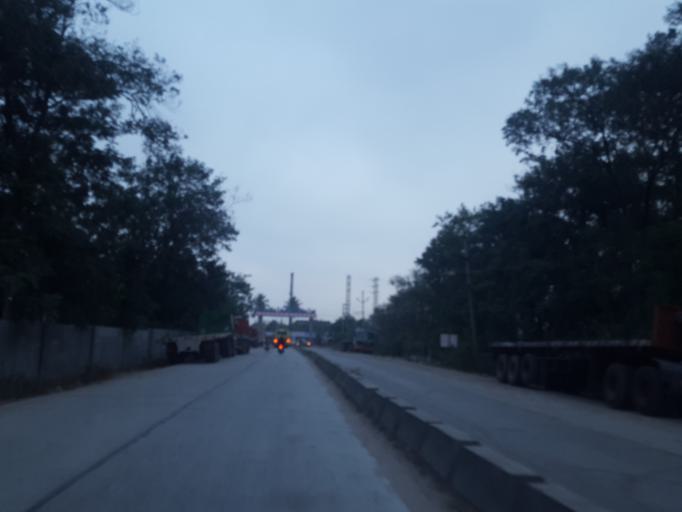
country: IN
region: Telangana
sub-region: Medak
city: Patancheru
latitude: 17.5304
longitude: 78.2541
